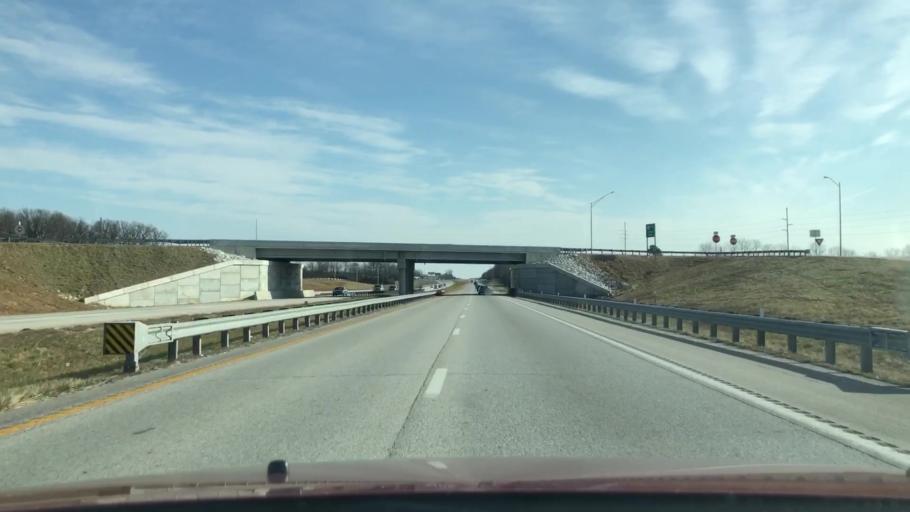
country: US
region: Missouri
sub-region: Christian County
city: Ozark
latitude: 37.1202
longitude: -93.1896
